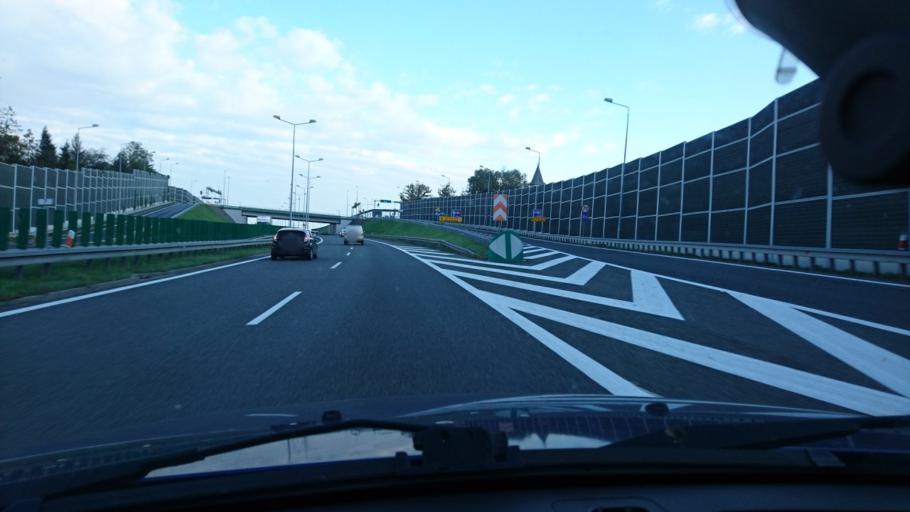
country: PL
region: Silesian Voivodeship
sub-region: Bielsko-Biala
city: Bielsko-Biala
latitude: 49.8217
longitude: 19.0870
